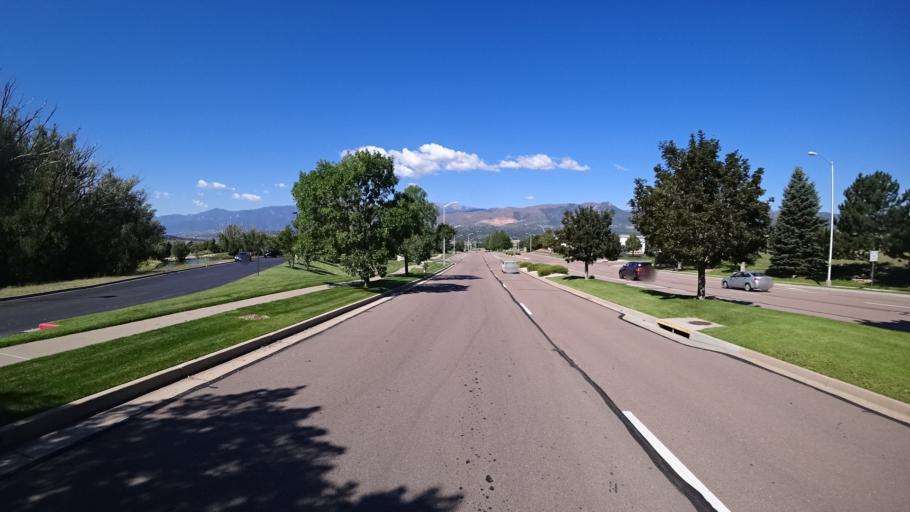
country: US
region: Colorado
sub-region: El Paso County
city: Air Force Academy
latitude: 38.9575
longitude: -104.7864
